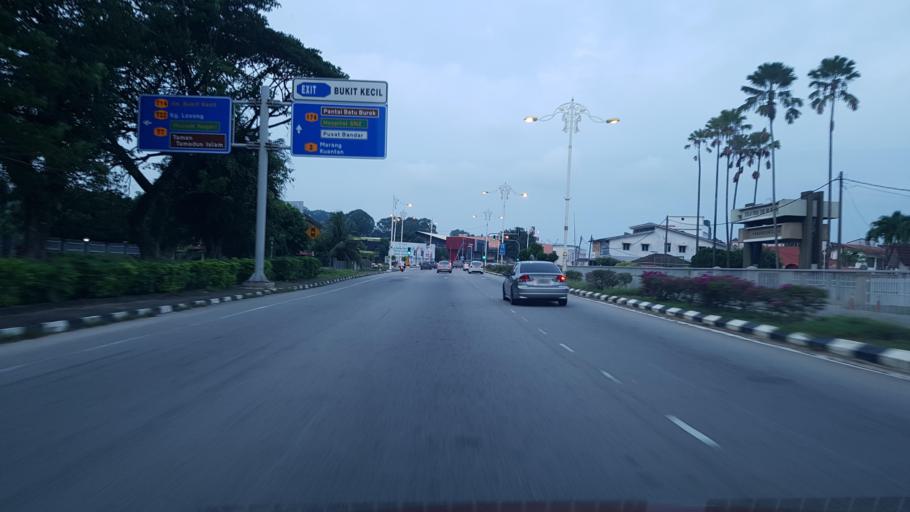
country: MY
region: Terengganu
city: Kuala Terengganu
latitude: 5.3128
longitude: 103.1365
